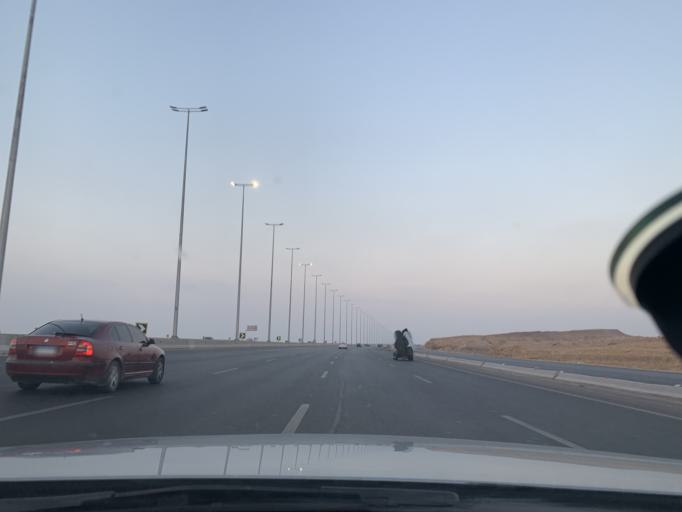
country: EG
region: Muhafazat al Qalyubiyah
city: Al Khankah
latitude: 30.0944
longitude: 31.4881
